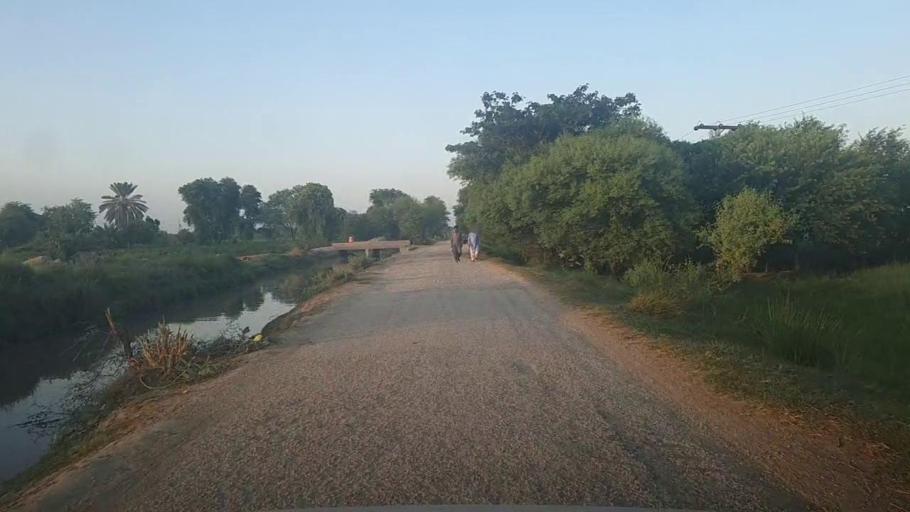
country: PK
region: Sindh
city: Khairpur
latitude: 28.0834
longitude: 69.7173
